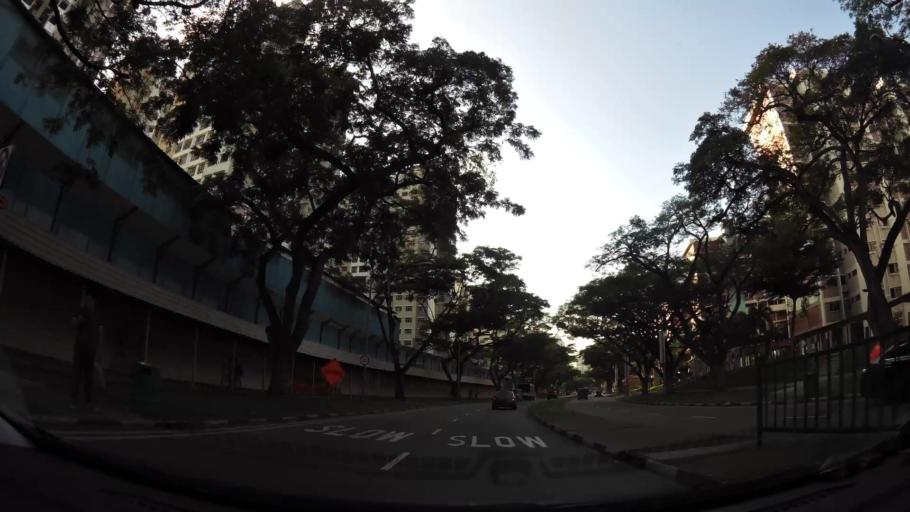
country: SG
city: Singapore
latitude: 1.3308
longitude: 103.9395
